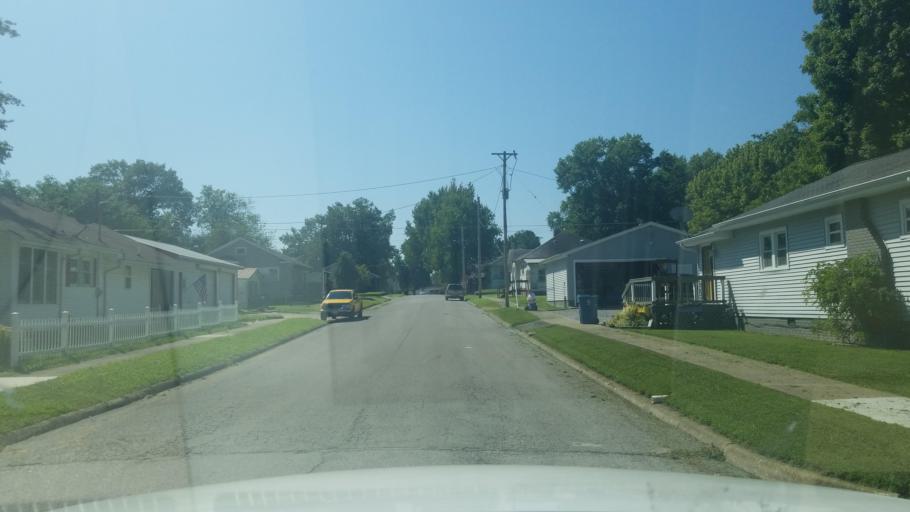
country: US
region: Illinois
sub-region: Saline County
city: Harrisburg
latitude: 37.7302
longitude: -88.5436
